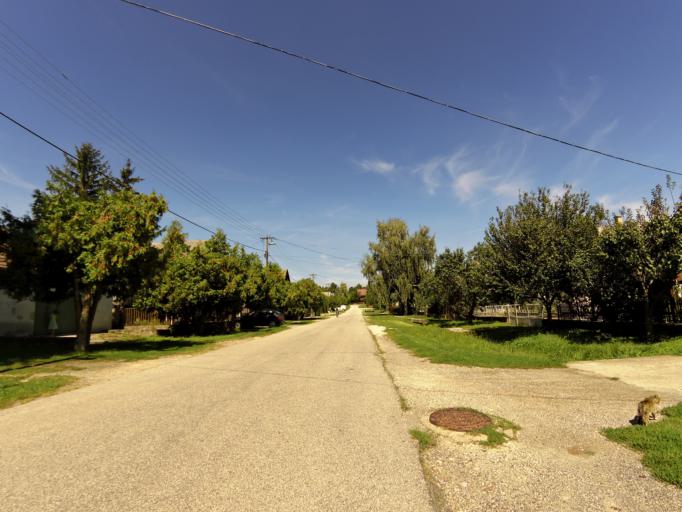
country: HU
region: Zala
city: Vonyarcvashegy
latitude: 46.8248
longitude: 17.3711
